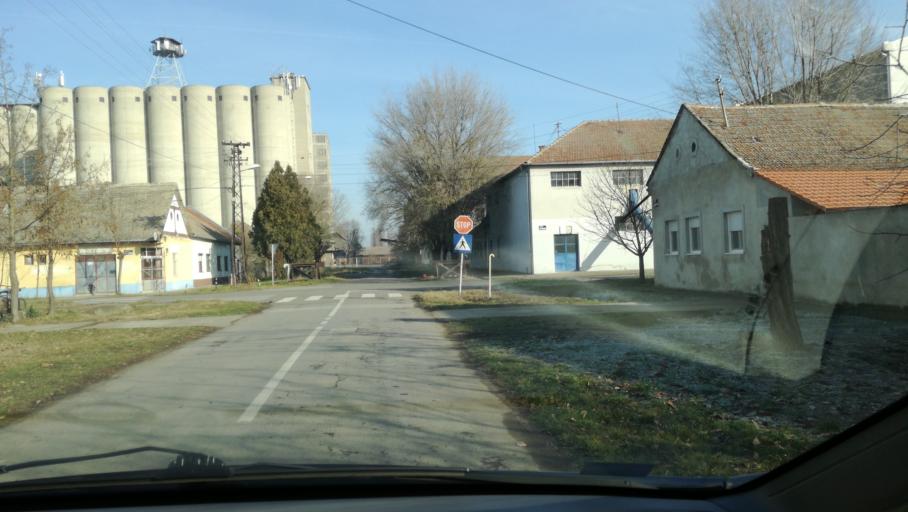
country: RS
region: Autonomna Pokrajina Vojvodina
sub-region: Severnobanatski Okrug
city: Kikinda
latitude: 45.8373
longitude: 20.4824
